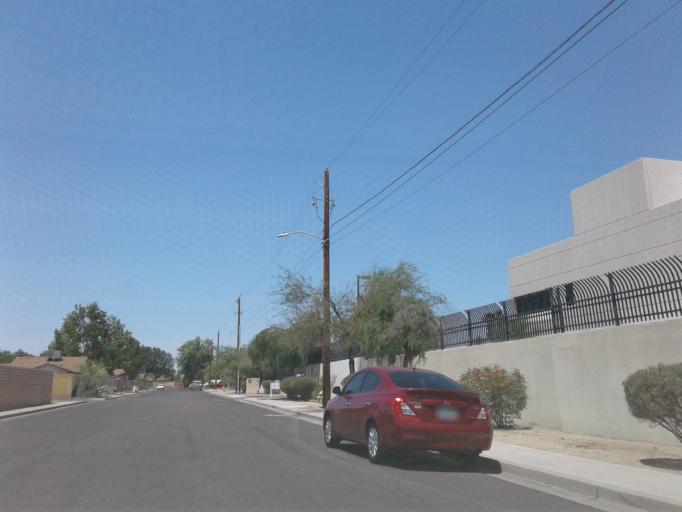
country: US
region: Arizona
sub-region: Maricopa County
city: Phoenix
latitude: 33.4739
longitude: -112.1065
